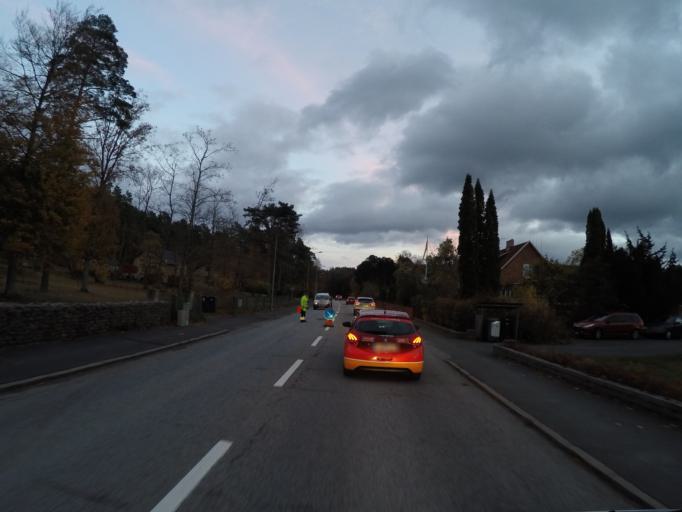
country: SE
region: Skane
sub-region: Kristianstads Kommun
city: Degeberga
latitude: 55.8288
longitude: 14.0921
